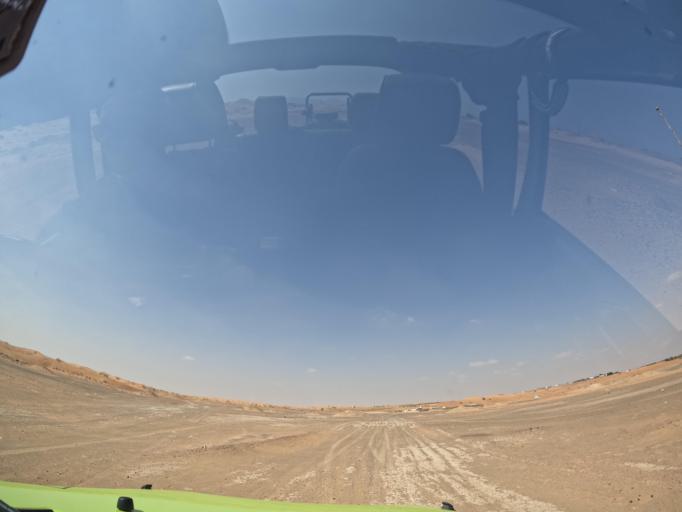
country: AE
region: Ash Shariqah
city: Adh Dhayd
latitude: 24.7964
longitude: 55.7873
